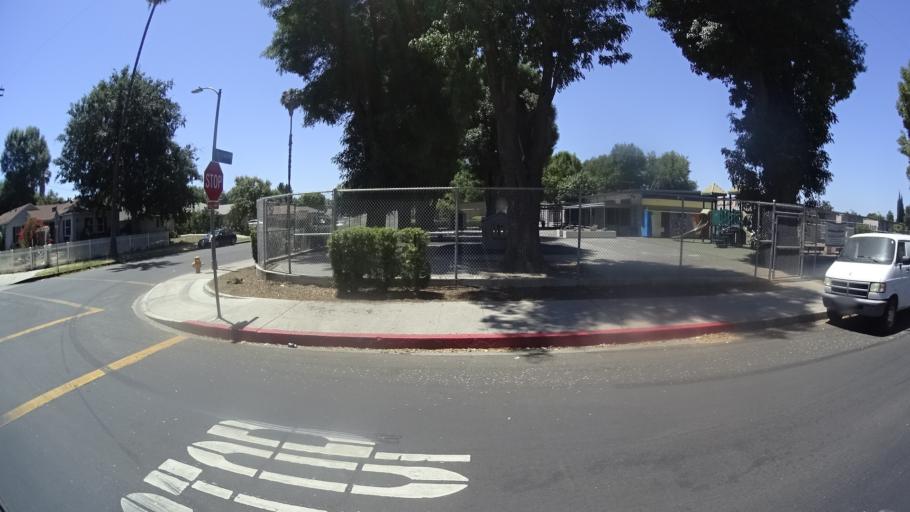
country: US
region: California
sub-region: Los Angeles County
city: Northridge
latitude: 34.1994
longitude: -118.5246
